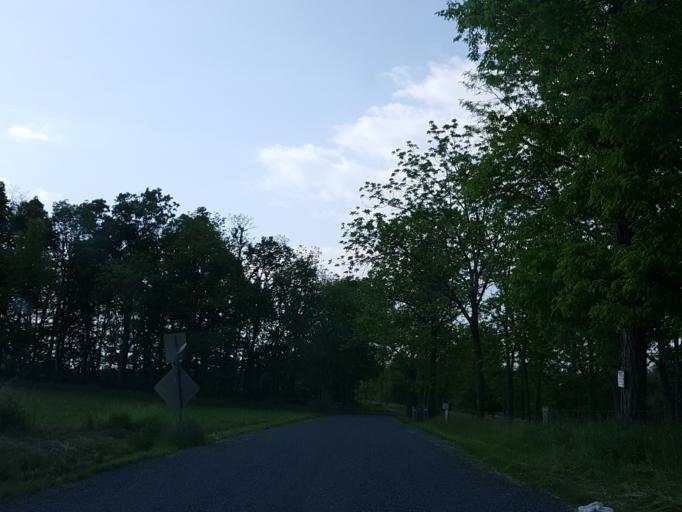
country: US
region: Pennsylvania
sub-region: Lebanon County
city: Campbelltown
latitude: 40.2151
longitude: -76.5717
